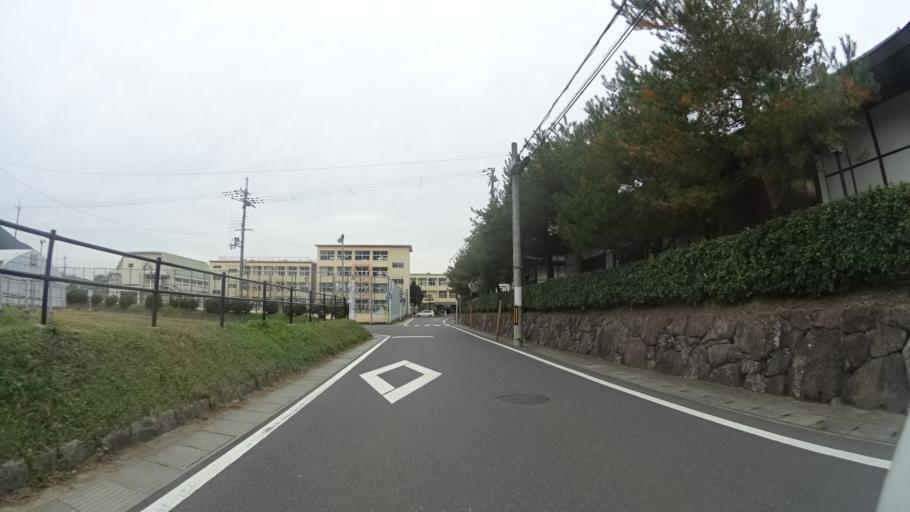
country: JP
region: Kyoto
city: Ayabe
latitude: 35.2938
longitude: 135.2596
